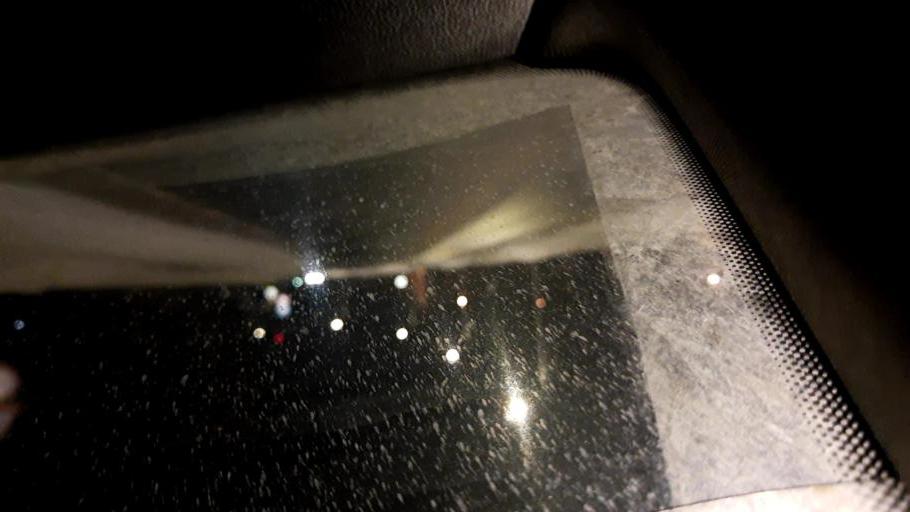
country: RU
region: Moskovskaya
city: Peresvet
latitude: 56.4172
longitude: 38.0987
